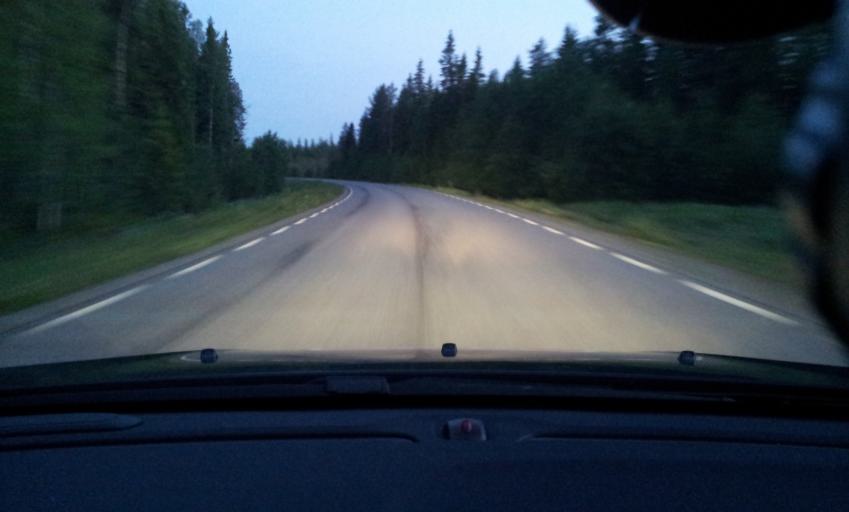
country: SE
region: Jaemtland
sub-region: Braecke Kommun
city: Braecke
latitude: 62.7506
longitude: 15.2477
